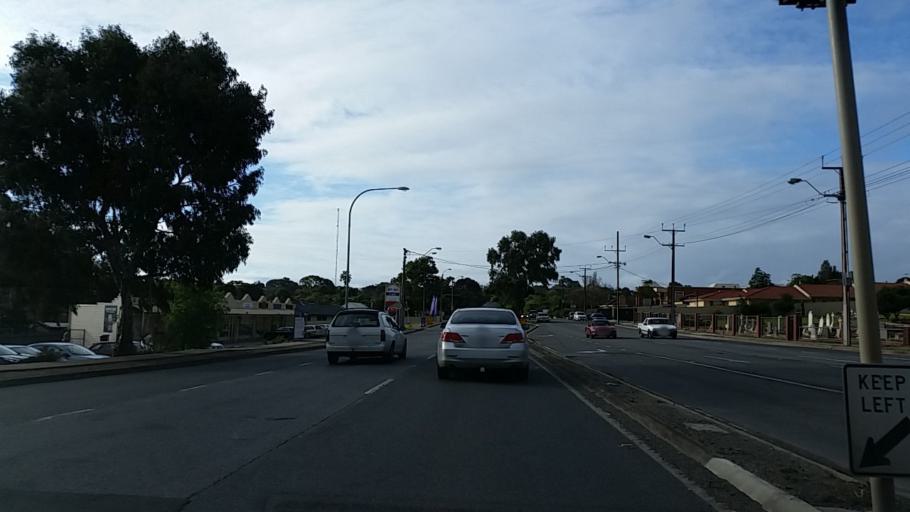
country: AU
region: South Australia
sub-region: Onkaparinga
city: Morphett Vale
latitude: -35.1157
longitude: 138.5227
